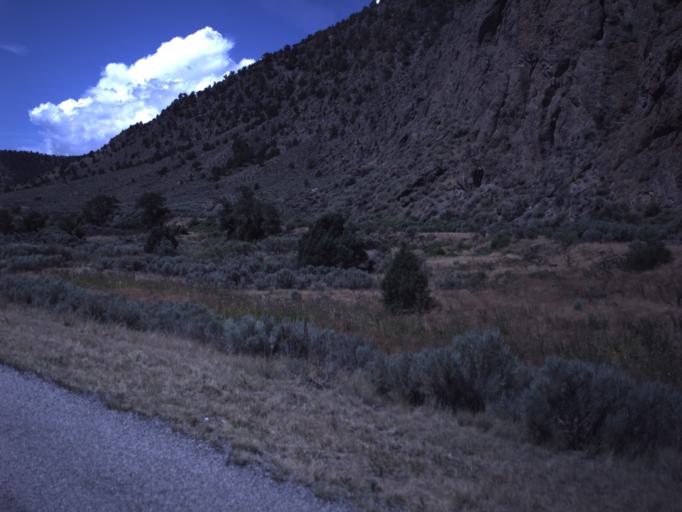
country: US
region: Utah
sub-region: Piute County
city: Junction
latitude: 38.0751
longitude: -112.3406
